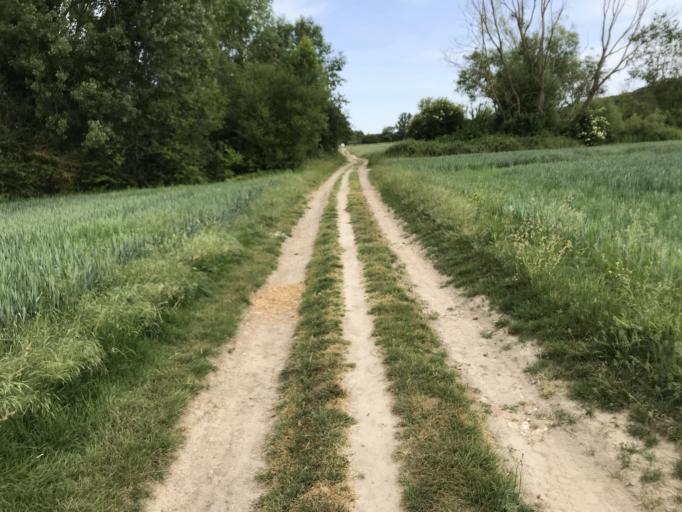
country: FR
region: Ile-de-France
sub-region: Departement de l'Essonne
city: Saulx-les-Chartreux
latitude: 48.6809
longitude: 2.2726
